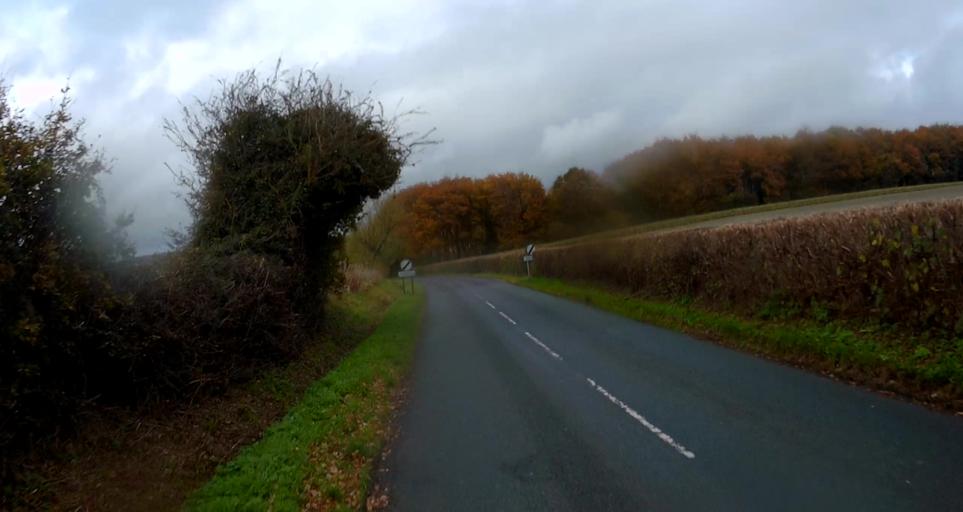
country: GB
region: England
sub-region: Hampshire
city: Four Marks
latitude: 51.1649
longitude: -1.0456
